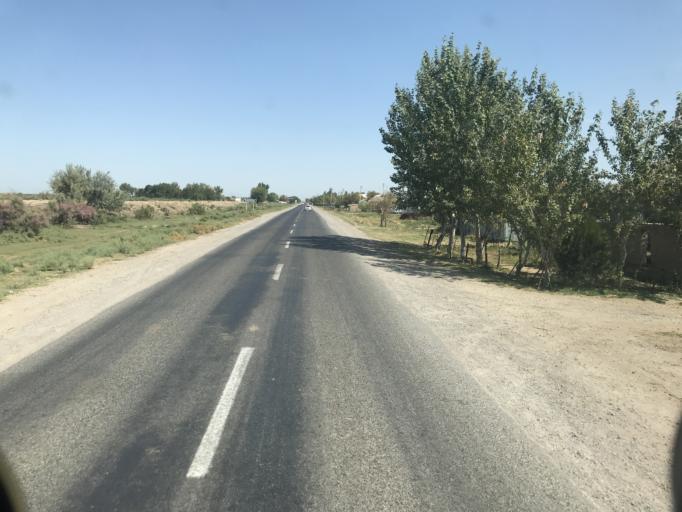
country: KZ
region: Ongtustik Qazaqstan
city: Myrzakent
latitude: 40.7553
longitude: 68.5370
